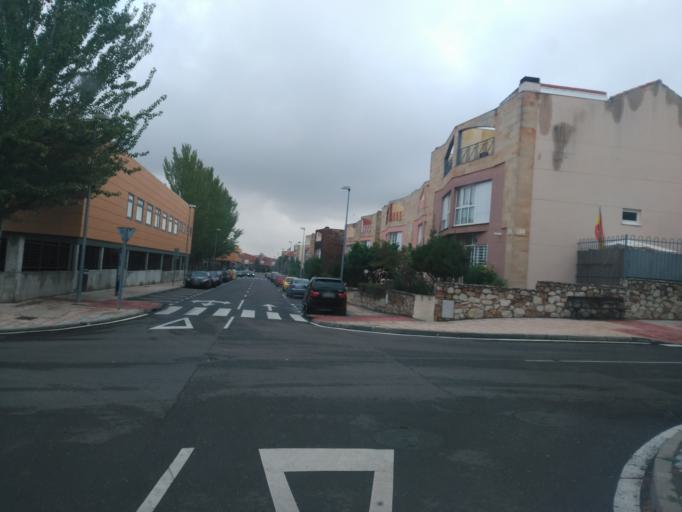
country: ES
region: Castille and Leon
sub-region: Provincia de Salamanca
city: Salamanca
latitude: 40.9510
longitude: -5.6811
